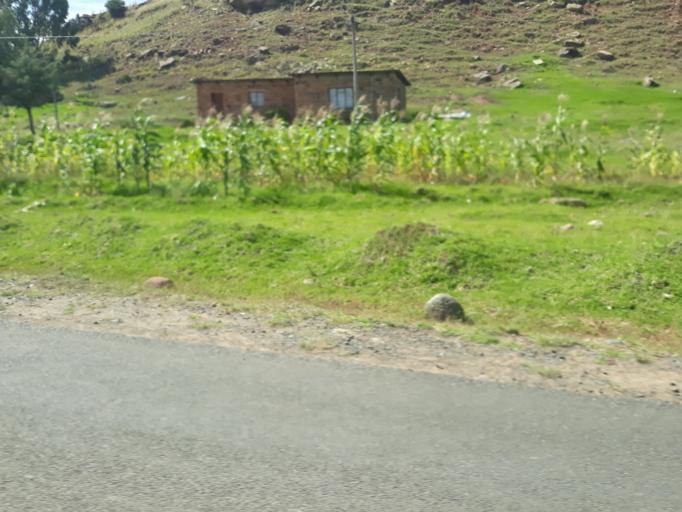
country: LS
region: Mohale's Hoek District
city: Mohale's Hoek
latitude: -30.1049
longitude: 27.4765
